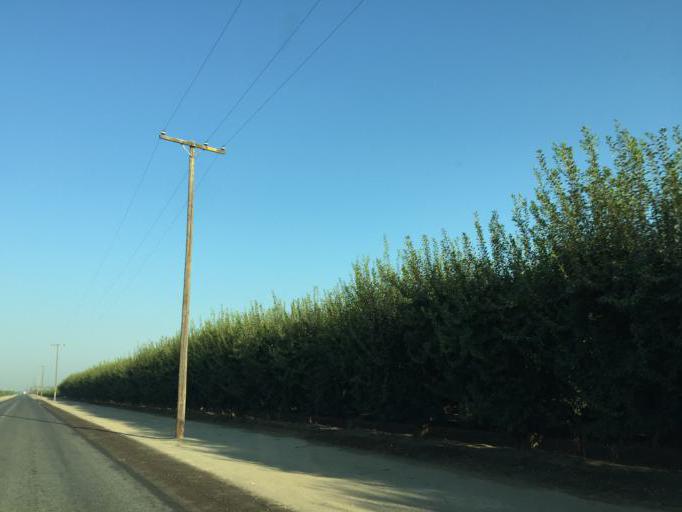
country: US
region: California
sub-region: Tulare County
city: London
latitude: 36.4589
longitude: -119.4409
